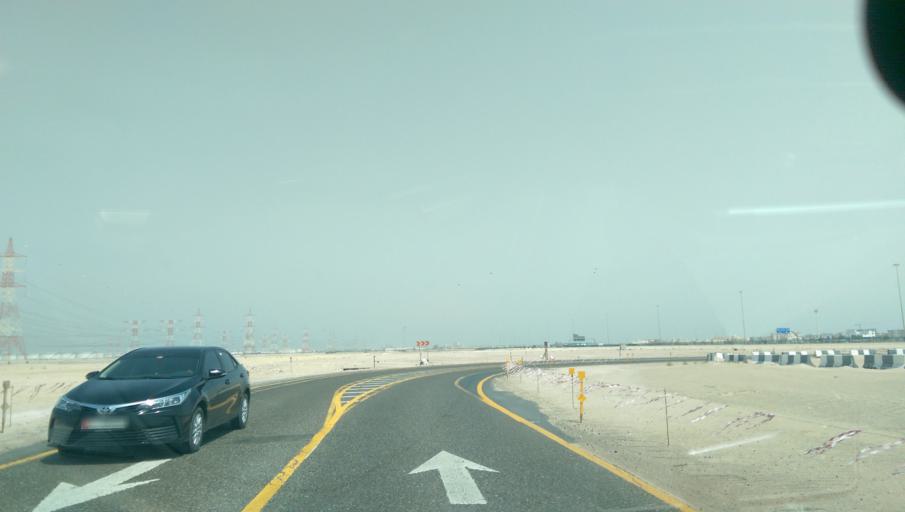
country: AE
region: Abu Dhabi
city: Abu Dhabi
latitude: 24.2979
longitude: 54.5383
